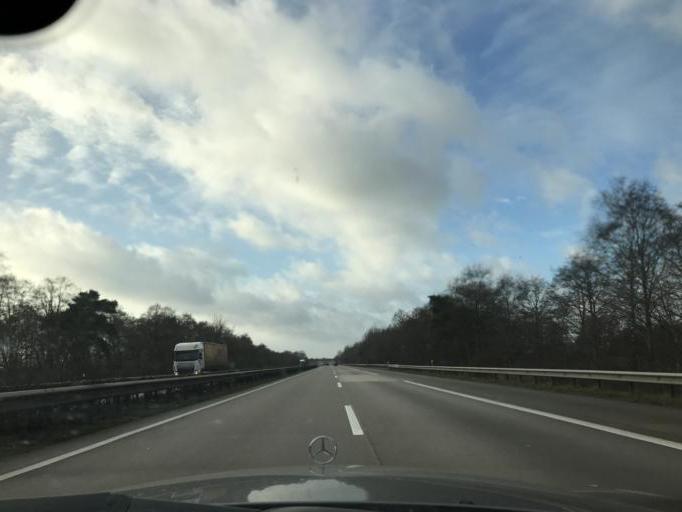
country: DE
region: Lower Saxony
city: Gross Ippener
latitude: 52.9861
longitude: 8.6421
